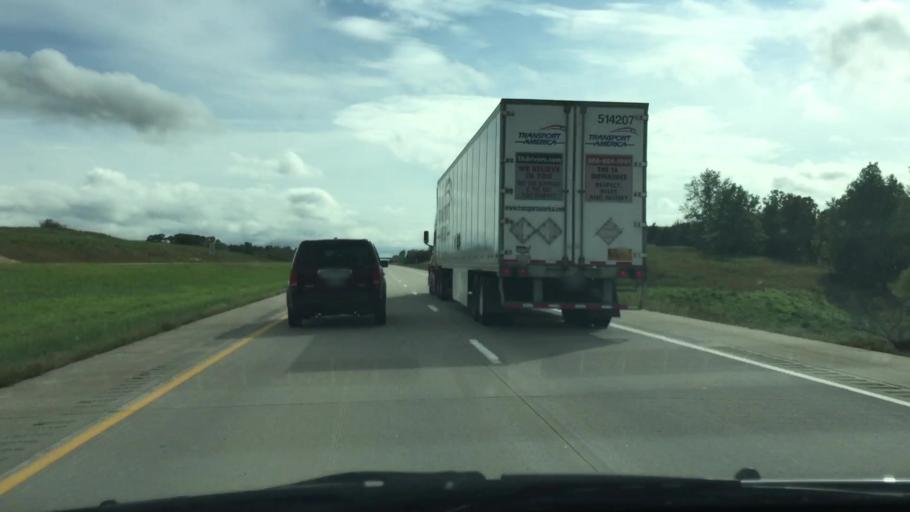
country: US
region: Iowa
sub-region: Decatur County
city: Leon
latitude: 40.8824
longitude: -93.8016
